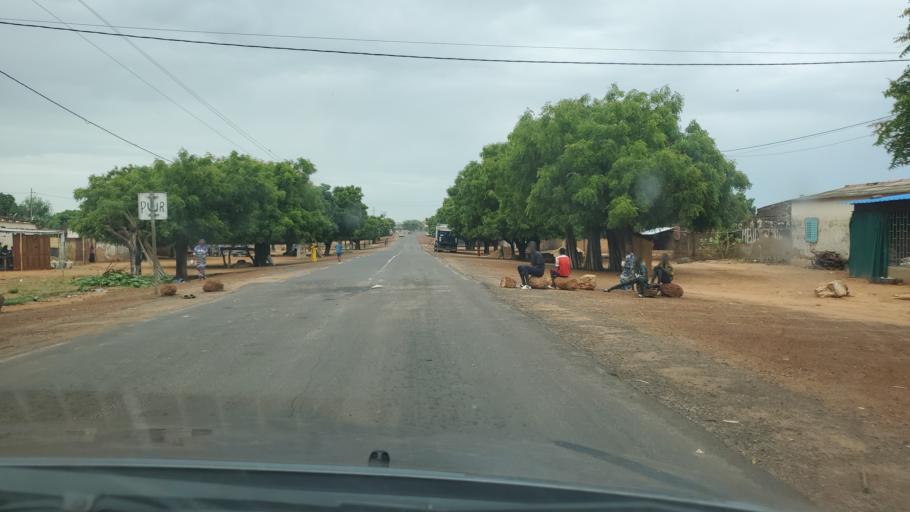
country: SN
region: Thies
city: Mekhe
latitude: 15.1302
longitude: -16.8605
